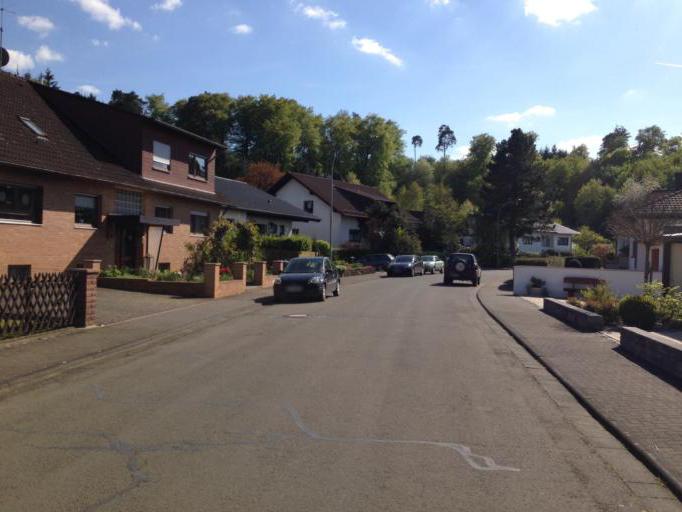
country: DE
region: Hesse
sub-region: Regierungsbezirk Giessen
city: Grunberg
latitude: 50.5548
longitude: 8.9018
